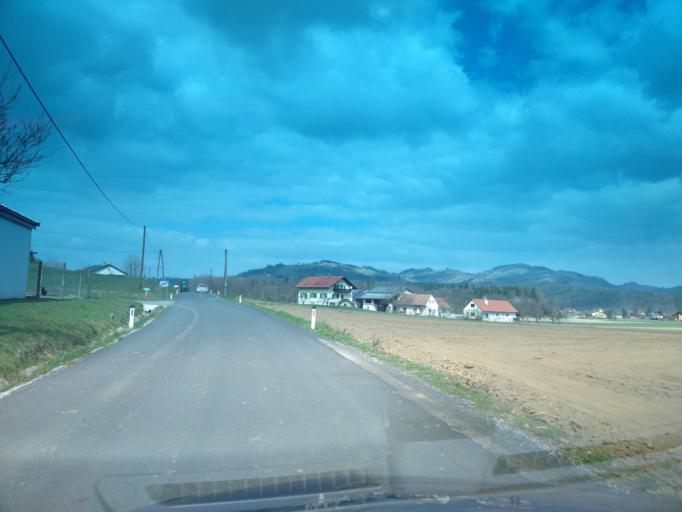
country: AT
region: Styria
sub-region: Politischer Bezirk Leibnitz
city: Grossklein
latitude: 46.7426
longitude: 15.4298
